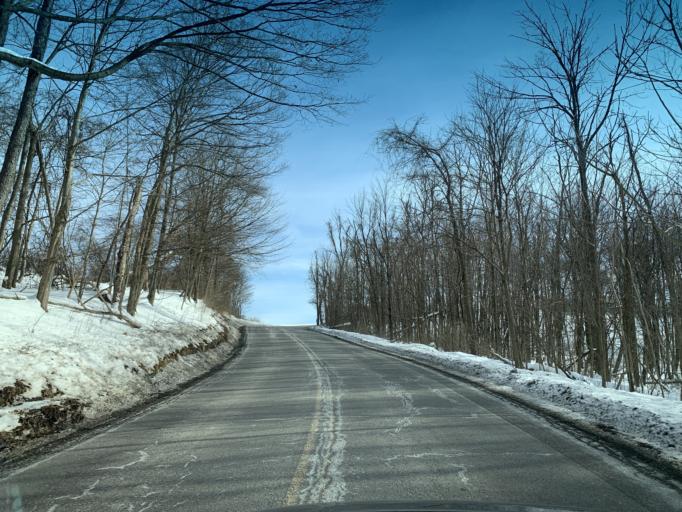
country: US
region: Maryland
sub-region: Allegany County
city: Frostburg
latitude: 39.6683
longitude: -78.8909
